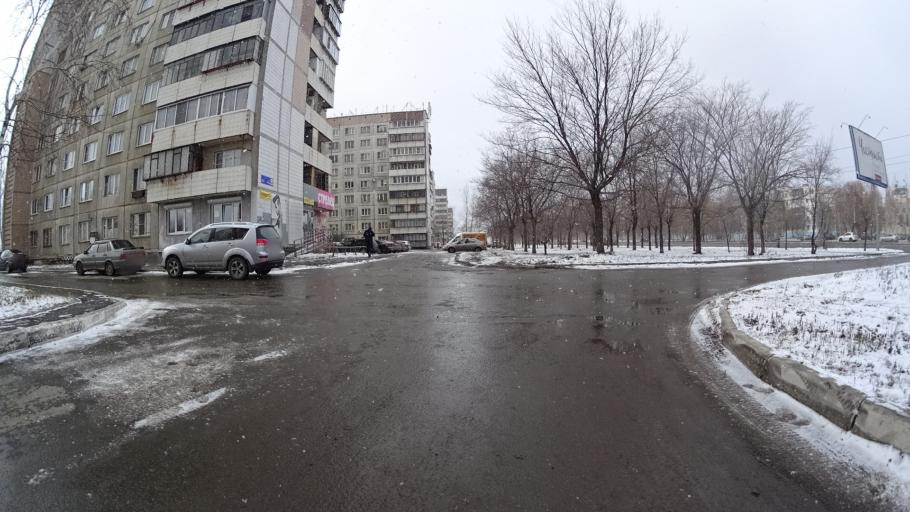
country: RU
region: Chelyabinsk
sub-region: Gorod Chelyabinsk
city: Chelyabinsk
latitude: 55.1882
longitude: 61.3175
